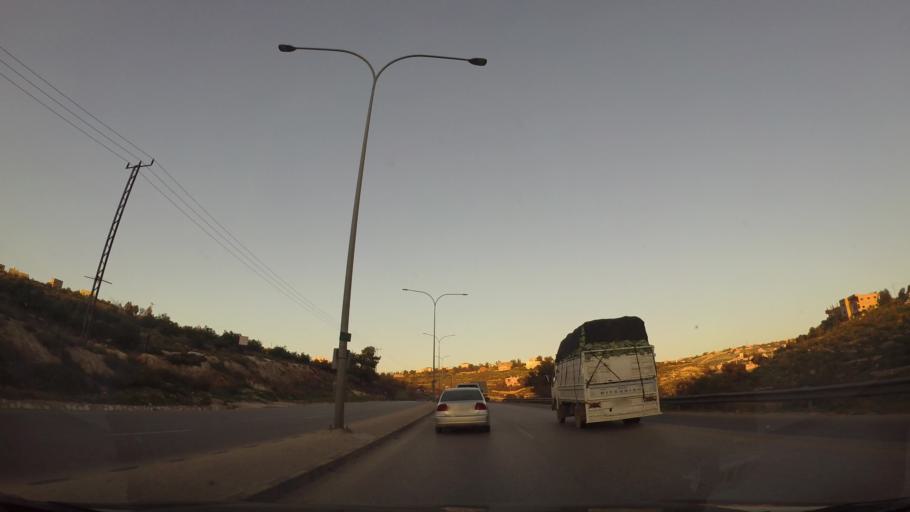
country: JO
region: Amman
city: Umm as Summaq
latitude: 31.8620
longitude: 35.7961
